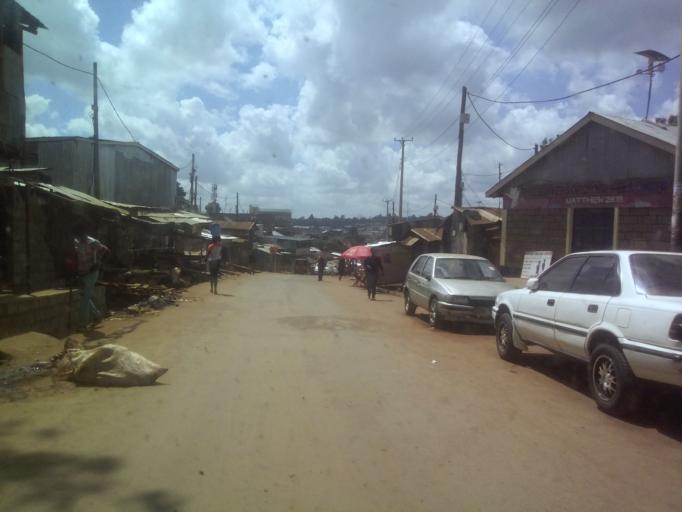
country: KE
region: Nairobi Area
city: Nairobi
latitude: -1.3121
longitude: 36.7751
